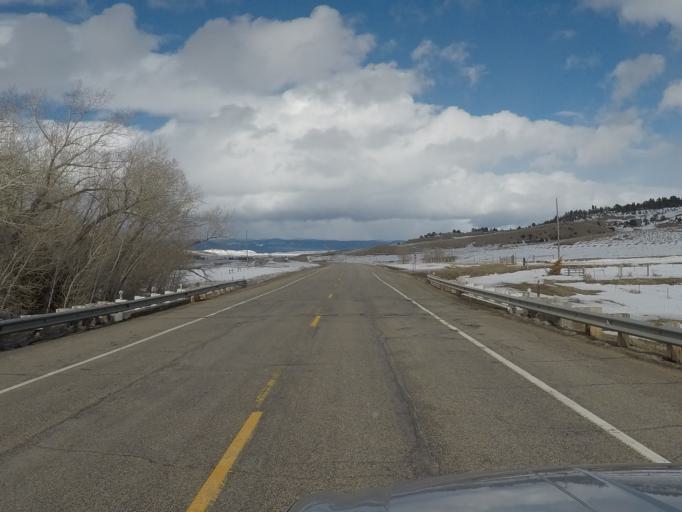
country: US
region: Montana
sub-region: Meagher County
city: White Sulphur Springs
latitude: 46.5853
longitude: -110.7924
